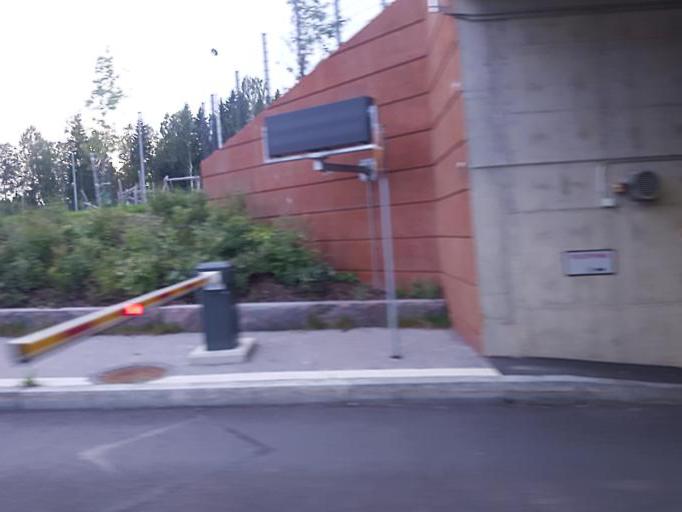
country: FI
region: Uusimaa
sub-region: Helsinki
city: Helsinki
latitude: 60.2551
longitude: 24.9179
